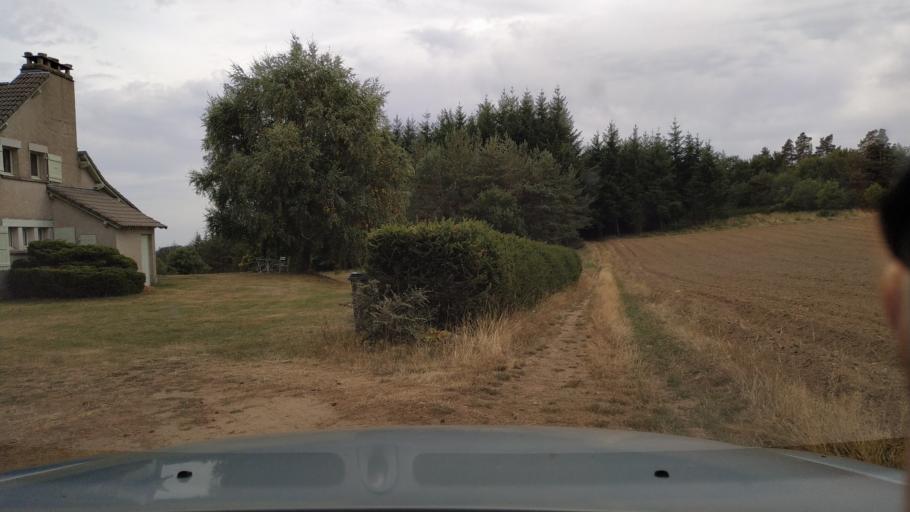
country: FR
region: Rhone-Alpes
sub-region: Departement de l'Ardeche
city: Saint-Agreve
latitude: 45.0241
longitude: 4.4391
